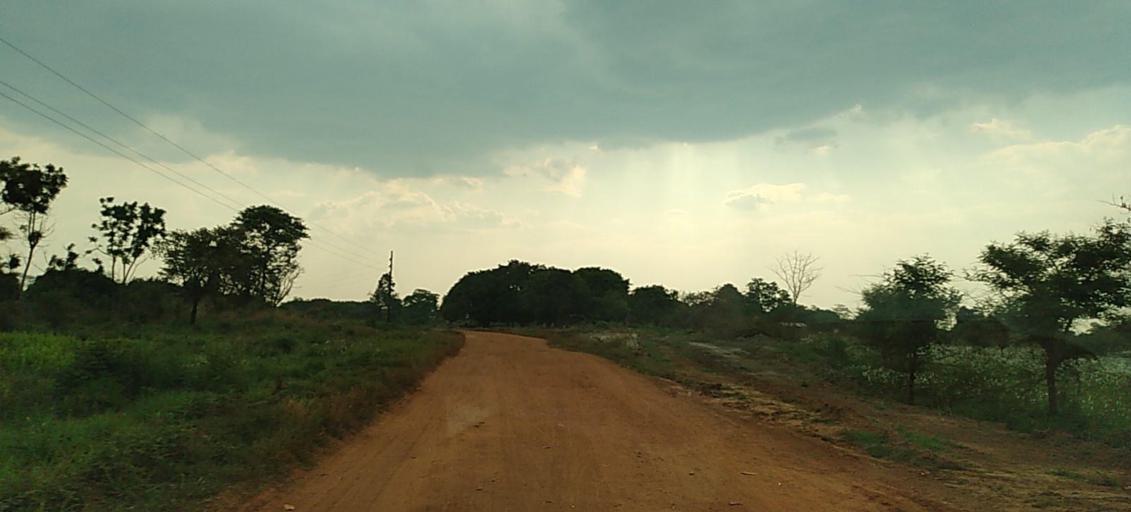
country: ZM
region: Copperbelt
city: Kalulushi
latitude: -12.9381
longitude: 27.9270
